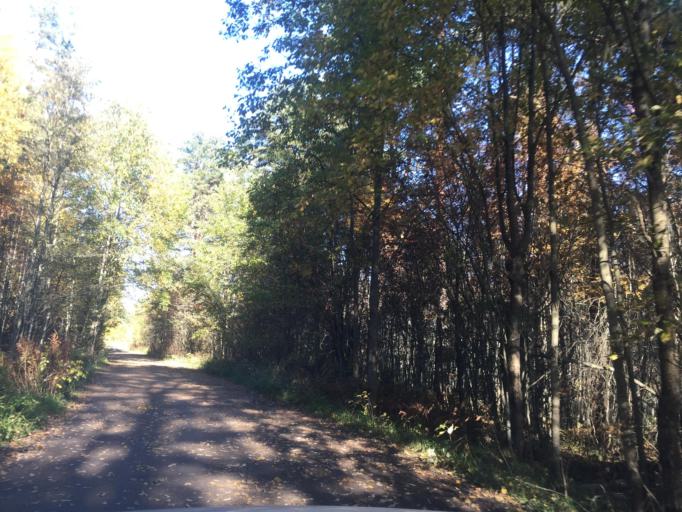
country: RU
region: Leningrad
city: Kuznechnoye
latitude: 61.2957
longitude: 30.0602
